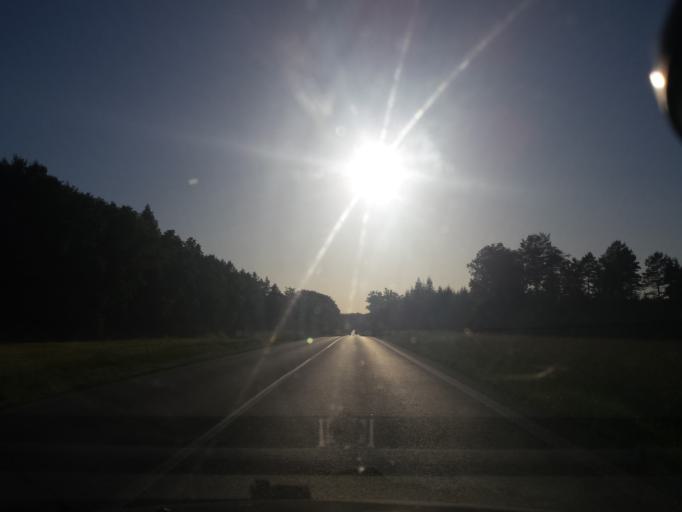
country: CZ
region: Liberecky
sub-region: Okres Ceska Lipa
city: Ceska Lipa
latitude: 50.6164
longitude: 14.5562
